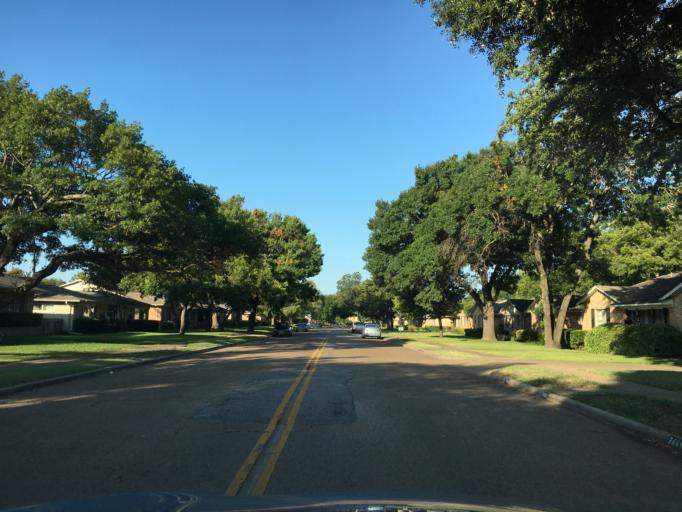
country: US
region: Texas
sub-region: Dallas County
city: Highland Park
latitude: 32.8562
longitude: -96.7349
